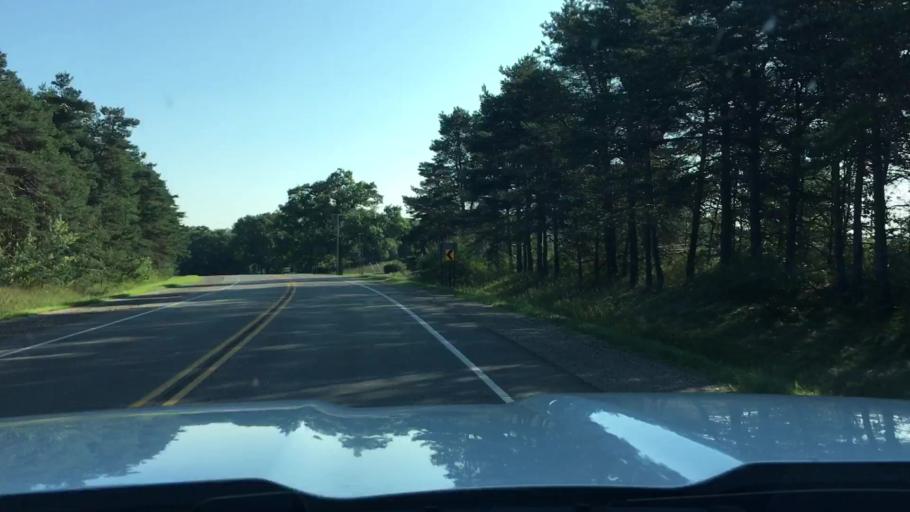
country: US
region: Michigan
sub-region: Kent County
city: Lowell
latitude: 42.9087
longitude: -85.3528
